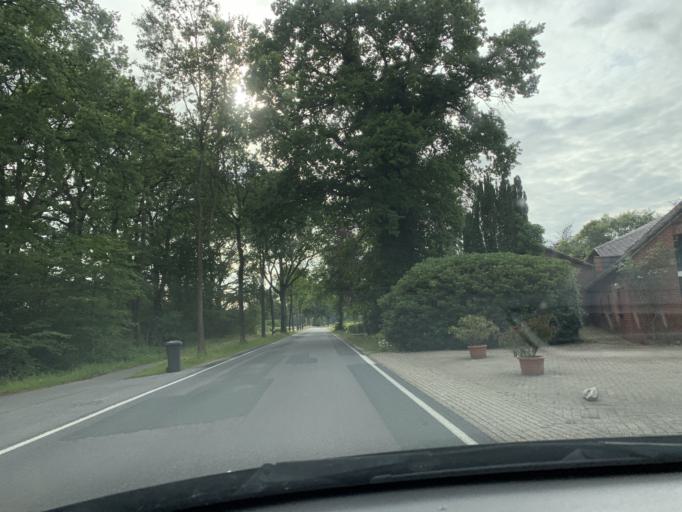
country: DE
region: Lower Saxony
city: Westerstede
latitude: 53.2755
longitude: 7.9327
